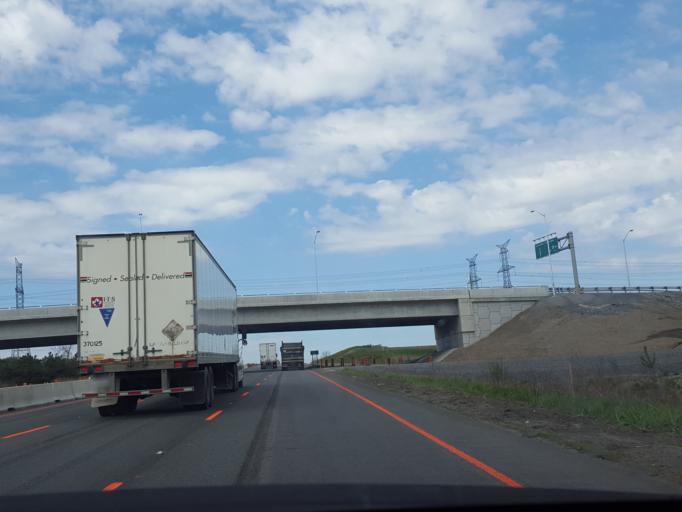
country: CA
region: Ontario
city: Oshawa
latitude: 43.8844
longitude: -78.7208
